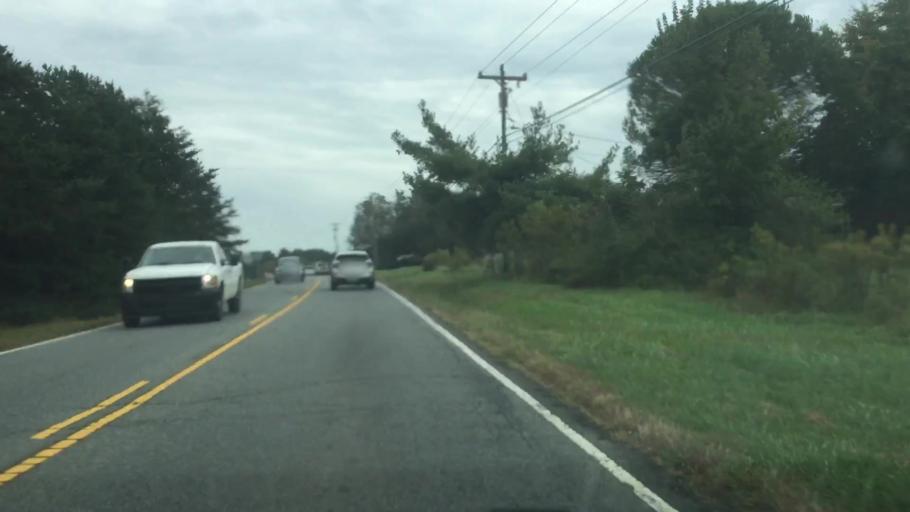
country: US
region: North Carolina
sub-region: Iredell County
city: Mooresville
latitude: 35.6412
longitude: -80.8381
